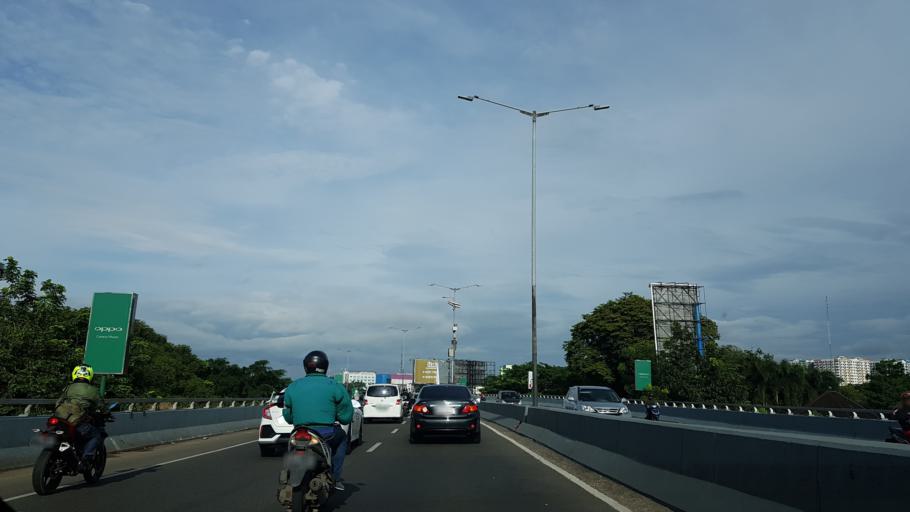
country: ID
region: West Java
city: Bandung
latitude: -6.8985
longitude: 107.6106
